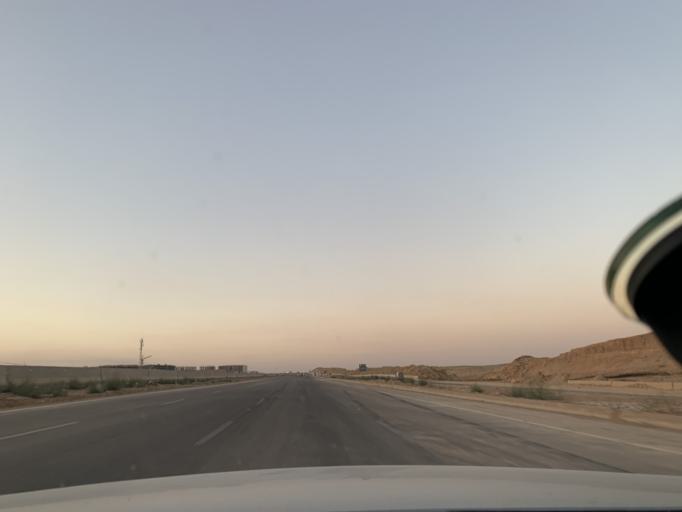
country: EG
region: Muhafazat al Qahirah
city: Halwan
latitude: 29.9595
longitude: 31.5448
